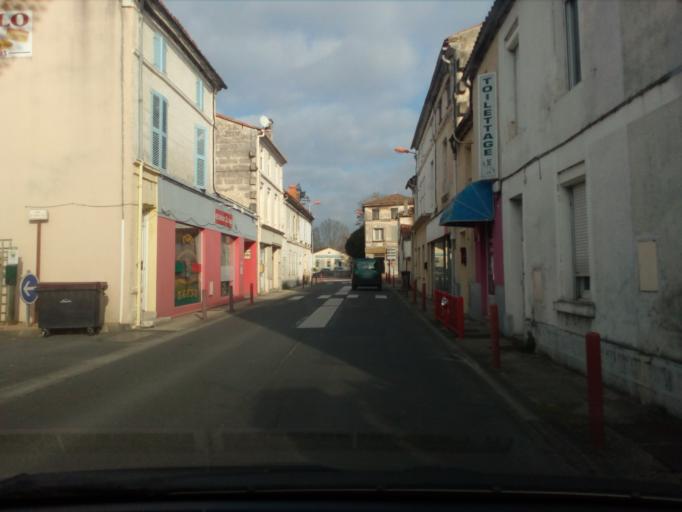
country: FR
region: Poitou-Charentes
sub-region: Departement de la Charente
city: Gond-Pontouvre
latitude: 45.6690
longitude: 0.1602
